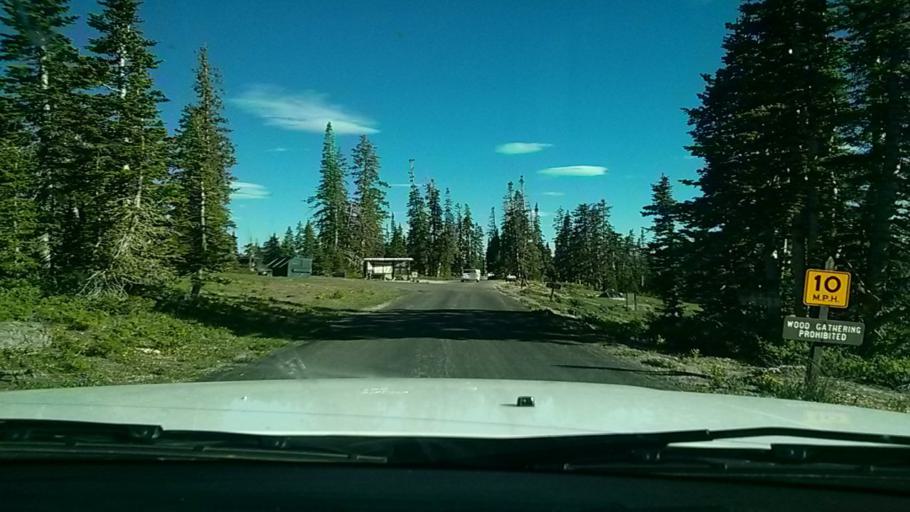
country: US
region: Utah
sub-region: Iron County
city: Parowan
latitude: 37.6117
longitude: -112.8316
